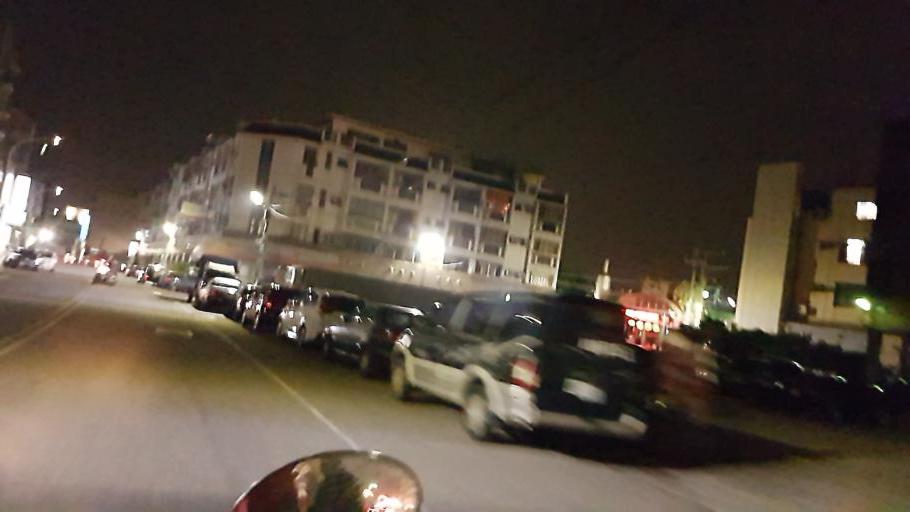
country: TW
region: Taiwan
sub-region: Changhua
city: Chang-hua
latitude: 24.0640
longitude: 120.5256
